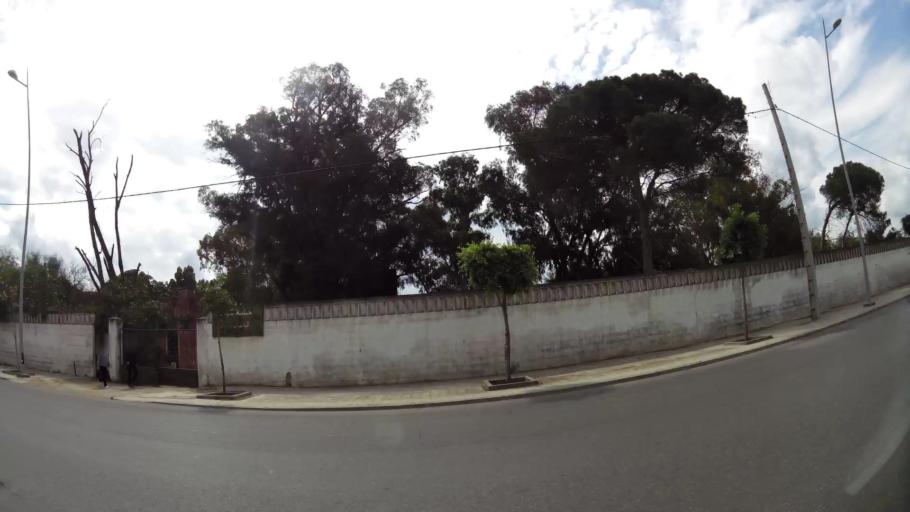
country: MA
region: Gharb-Chrarda-Beni Hssen
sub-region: Kenitra Province
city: Kenitra
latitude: 34.2559
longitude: -6.5689
